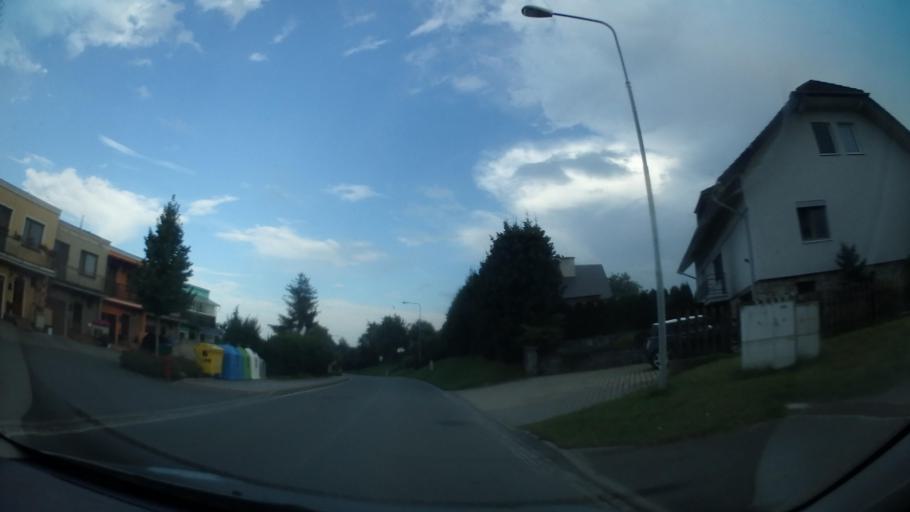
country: CZ
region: Olomoucky
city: Zabreh
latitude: 49.8860
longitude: 16.8541
